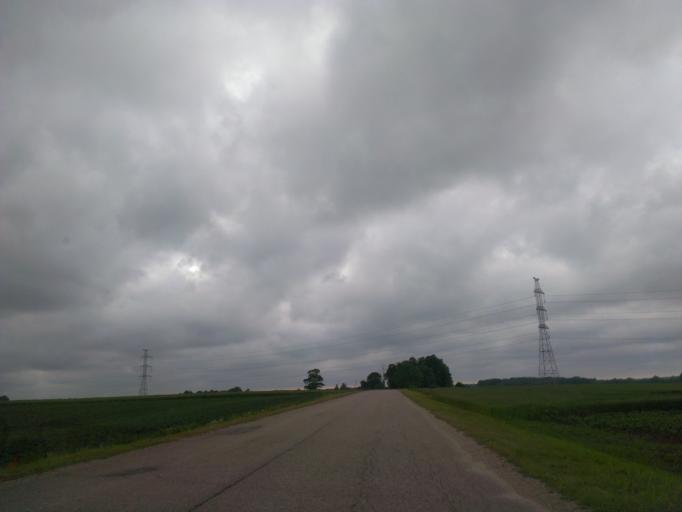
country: LV
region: Aizpute
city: Aizpute
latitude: 56.7221
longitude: 21.4386
